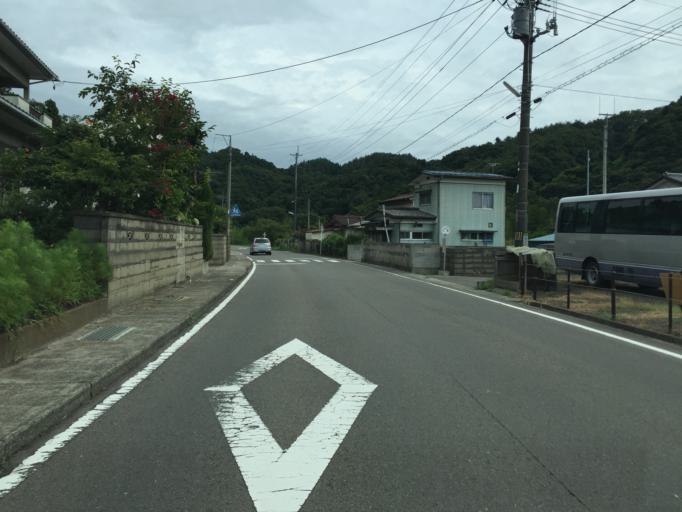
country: JP
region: Fukushima
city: Fukushima-shi
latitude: 37.7195
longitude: 140.4736
